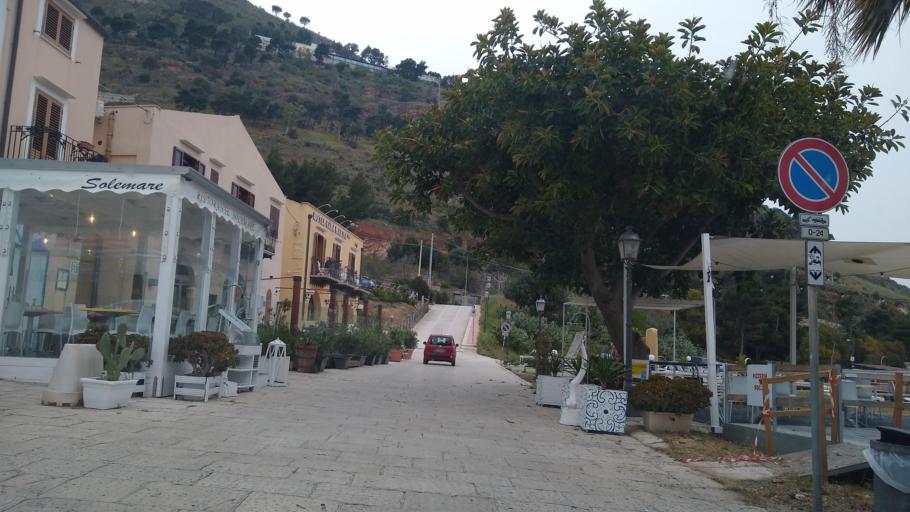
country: IT
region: Sicily
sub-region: Trapani
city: Castellammare del Golfo
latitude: 38.0282
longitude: 12.8792
